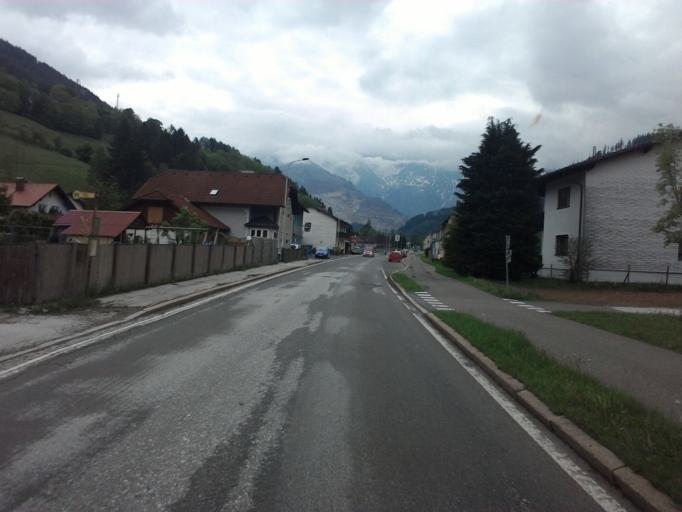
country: AT
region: Styria
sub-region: Politischer Bezirk Leoben
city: Eisenerz
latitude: 47.5571
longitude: 14.8696
